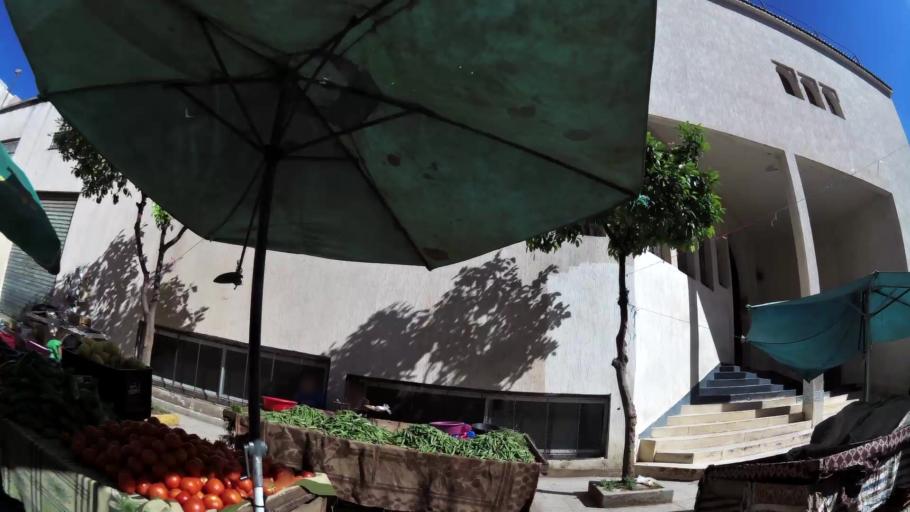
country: MA
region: Fes-Boulemane
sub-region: Fes
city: Fes
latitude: 34.0145
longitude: -4.9763
